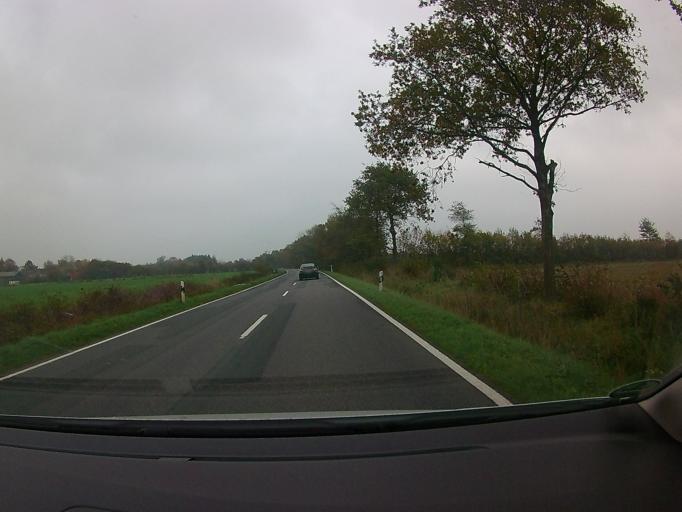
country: DE
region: Schleswig-Holstein
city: Wanderup
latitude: 54.6974
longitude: 9.3151
